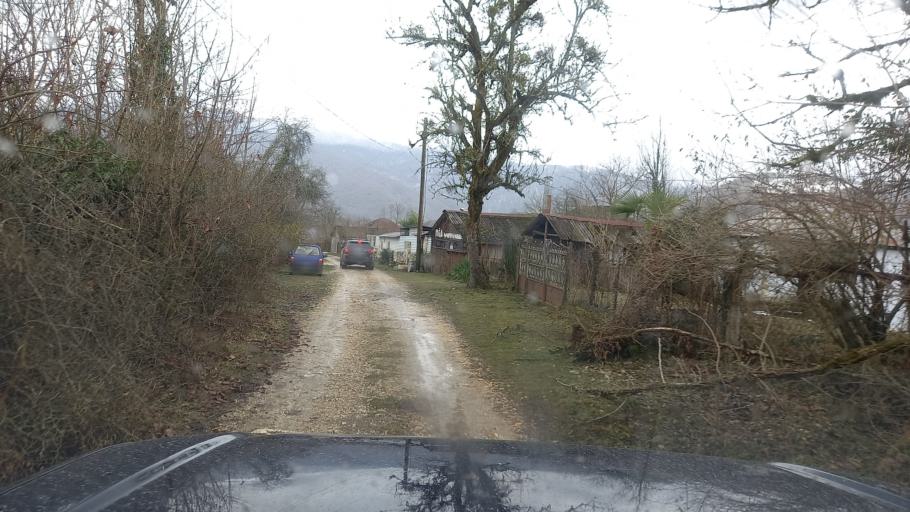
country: GE
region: Abkhazia
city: Dranda
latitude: 43.0350
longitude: 41.3265
